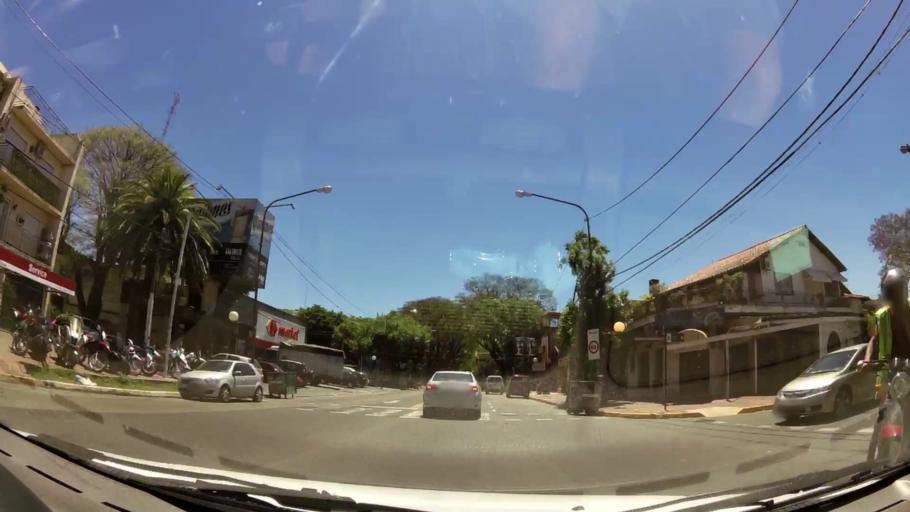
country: AR
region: Buenos Aires
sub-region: Partido de Vicente Lopez
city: Olivos
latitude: -34.4906
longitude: -58.4847
